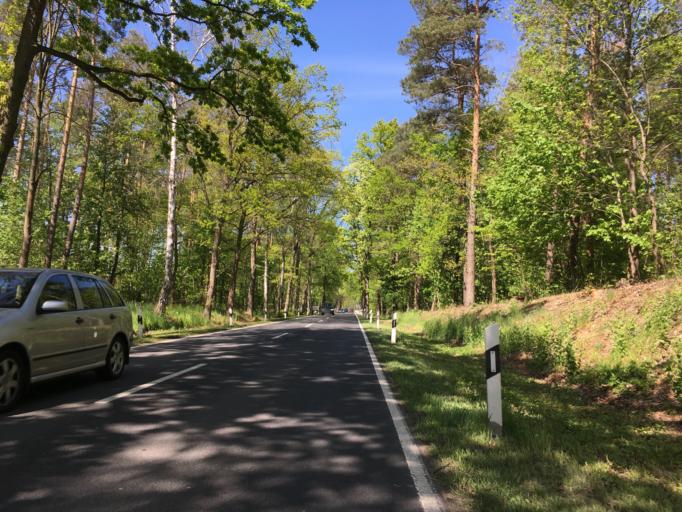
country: DE
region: Brandenburg
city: Rudnitz
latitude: 52.7670
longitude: 13.5653
